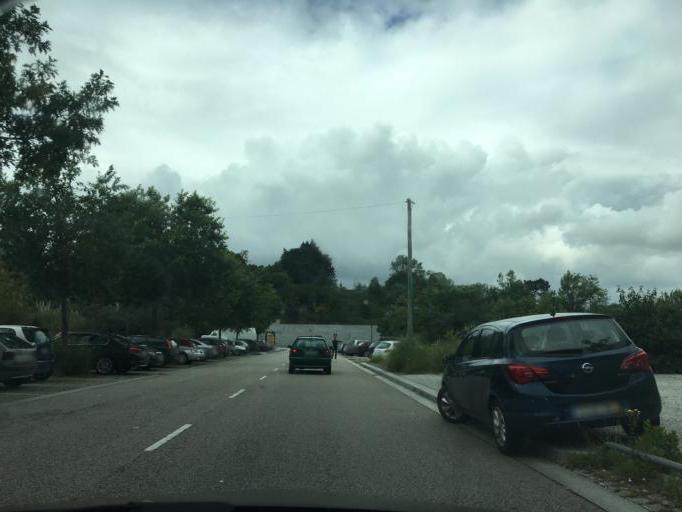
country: PT
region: Porto
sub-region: Porto
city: Porto
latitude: 41.1639
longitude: -8.5858
